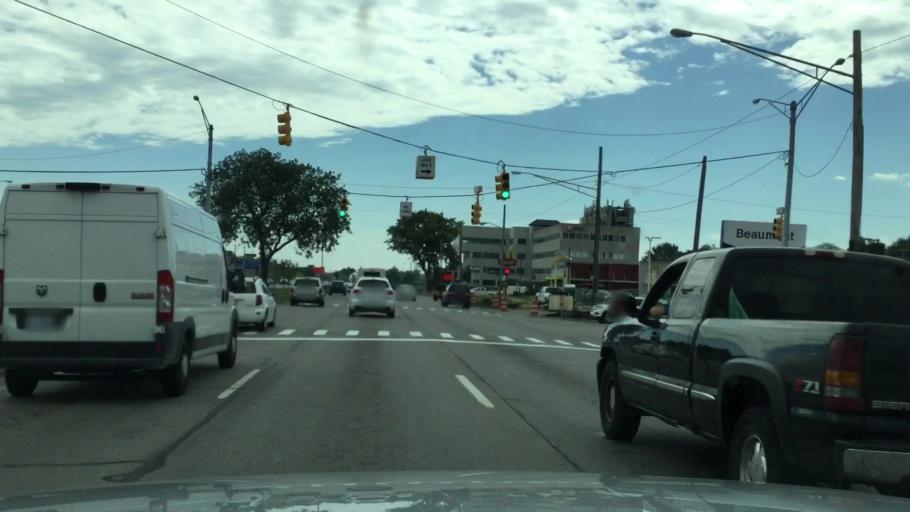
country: US
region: Michigan
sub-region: Oakland County
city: Berkley
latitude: 42.5169
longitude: -83.1854
